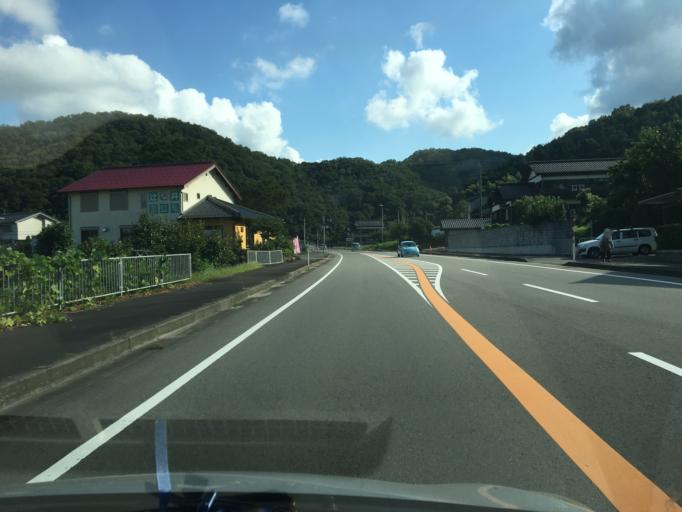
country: JP
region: Hyogo
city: Toyooka
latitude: 35.4552
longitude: 134.7691
